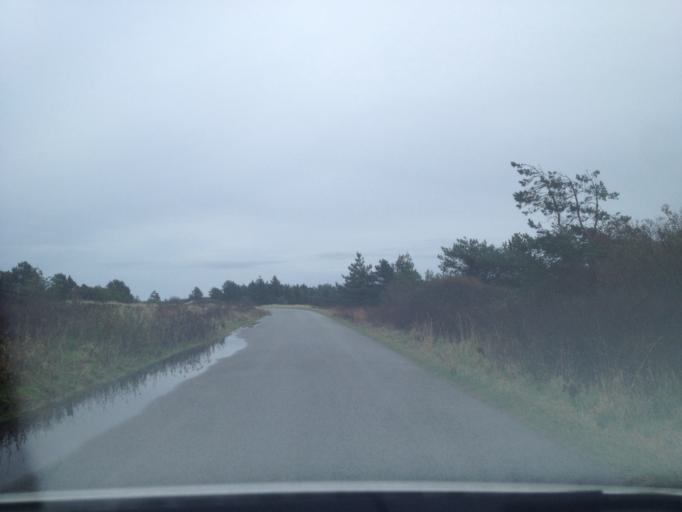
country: DE
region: Schleswig-Holstein
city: List
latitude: 55.1588
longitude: 8.5396
